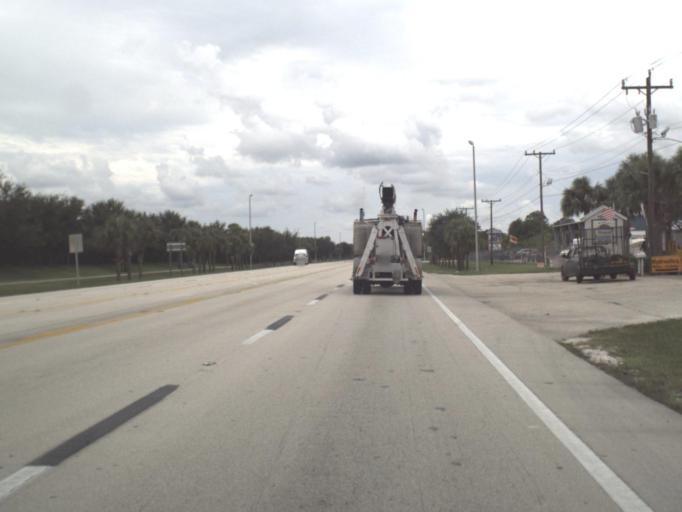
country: US
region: Florida
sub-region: Lee County
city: Fort Myers Shores
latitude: 26.7072
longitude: -81.7341
